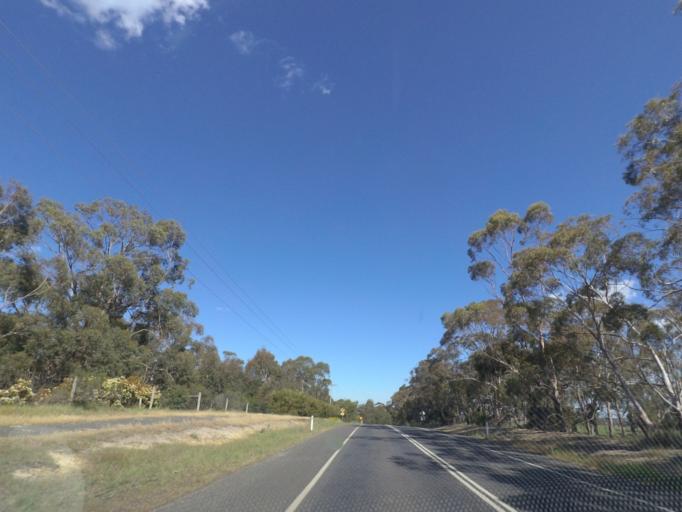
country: AU
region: Victoria
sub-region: Moorabool
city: Bacchus Marsh
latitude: -37.5718
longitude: 144.3140
